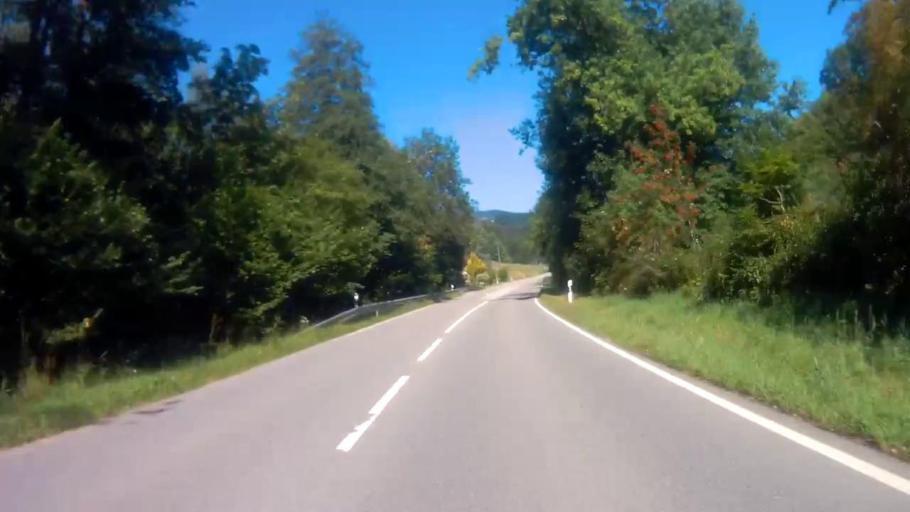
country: DE
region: Baden-Wuerttemberg
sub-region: Freiburg Region
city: Hausen
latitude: 47.7197
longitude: 7.7925
